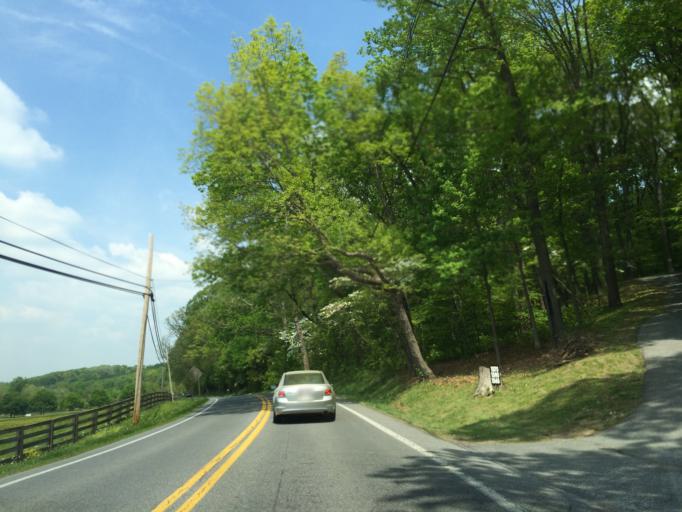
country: US
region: Maryland
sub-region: Carroll County
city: Sykesville
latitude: 39.3224
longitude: -76.8981
